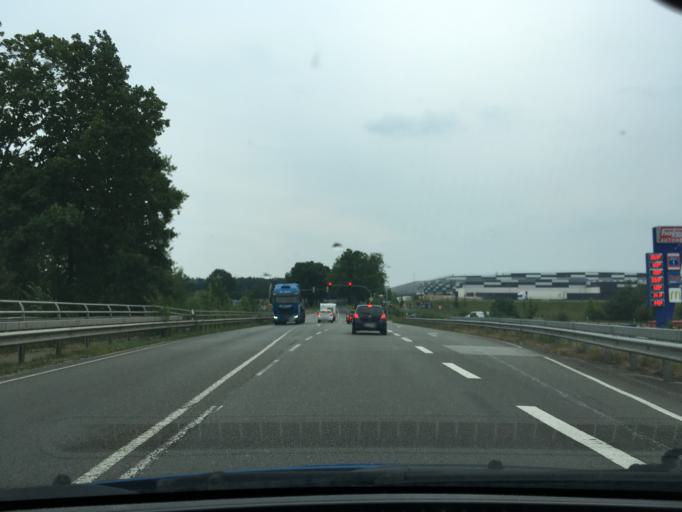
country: DE
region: Lower Saxony
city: Wenzendorf
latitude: 53.3708
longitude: 9.8048
